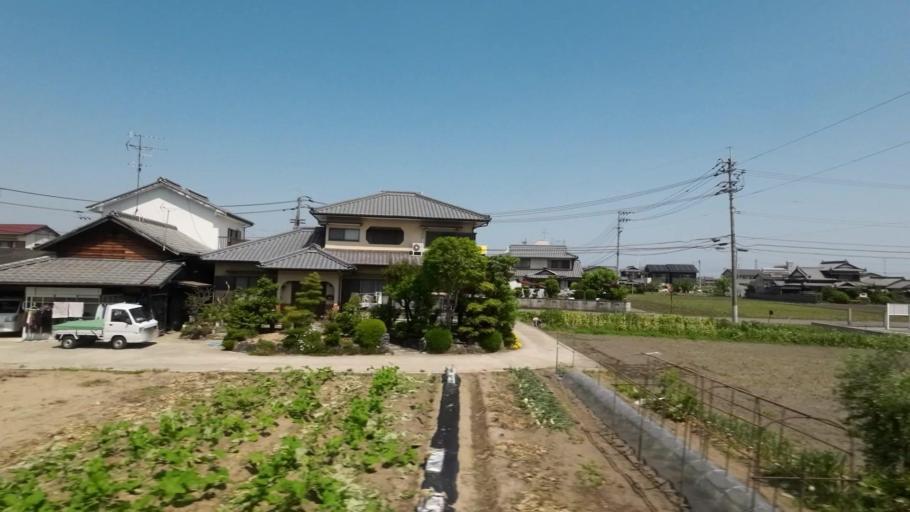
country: JP
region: Ehime
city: Saijo
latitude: 33.8991
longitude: 133.1707
